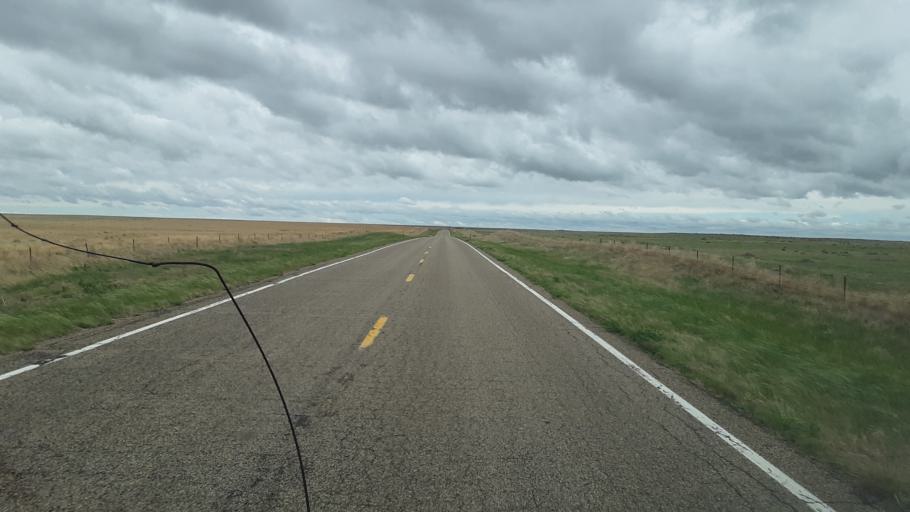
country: US
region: Colorado
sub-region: Lincoln County
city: Hugo
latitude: 38.8509
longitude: -103.5943
